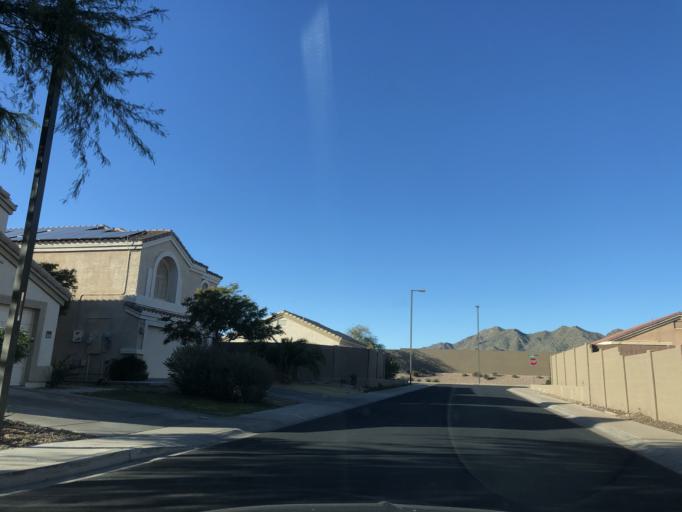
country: US
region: Arizona
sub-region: Maricopa County
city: Buckeye
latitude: 33.4393
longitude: -112.5692
